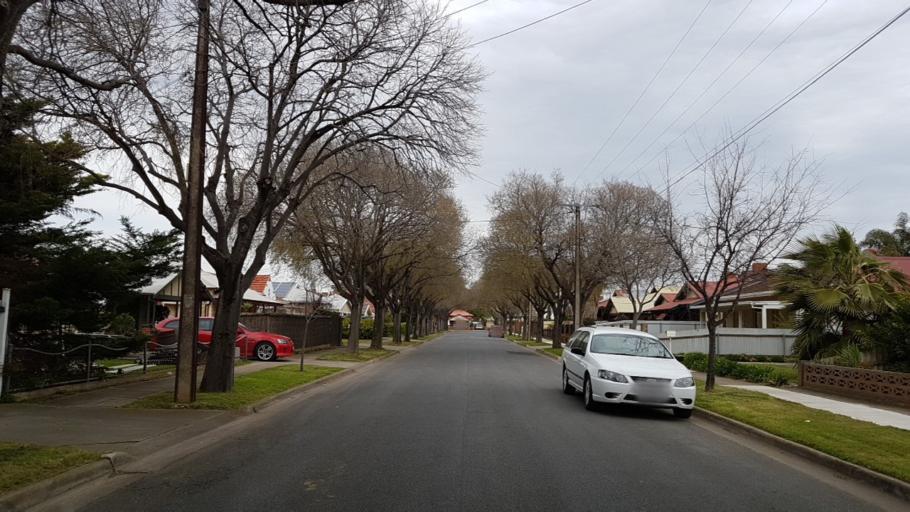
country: AU
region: South Australia
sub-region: Charles Sturt
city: Allenby Gardens
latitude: -34.8993
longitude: 138.5529
